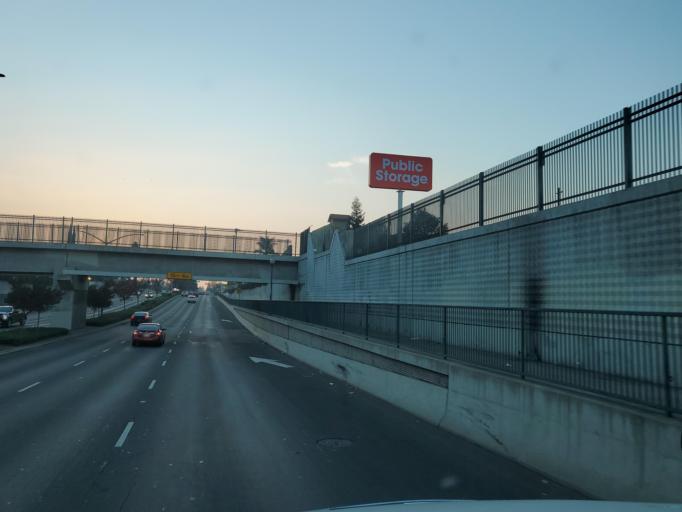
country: US
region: California
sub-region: San Joaquin County
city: Lincoln Village
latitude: 38.0015
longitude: -121.2938
